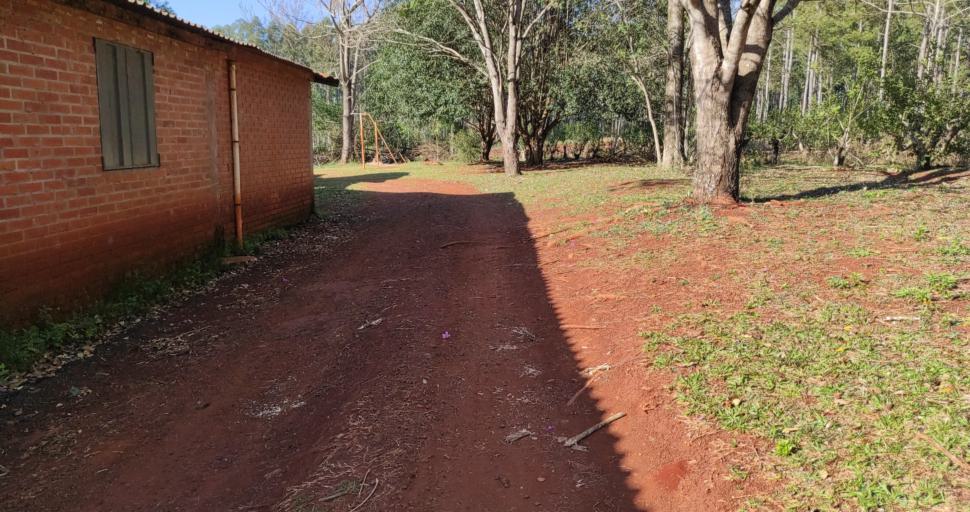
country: AR
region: Misiones
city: Capiovi
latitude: -26.8715
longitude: -55.0430
